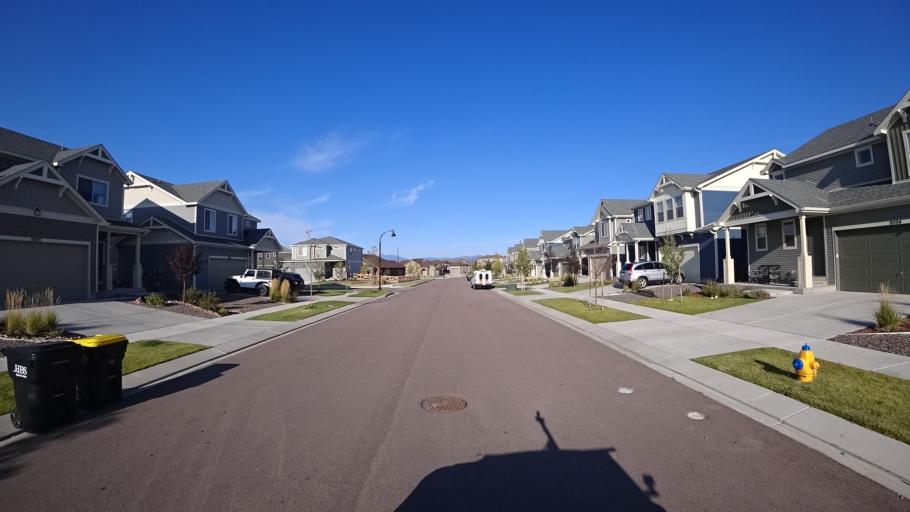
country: US
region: Colorado
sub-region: El Paso County
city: Cimarron Hills
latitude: 38.9358
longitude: -104.6576
